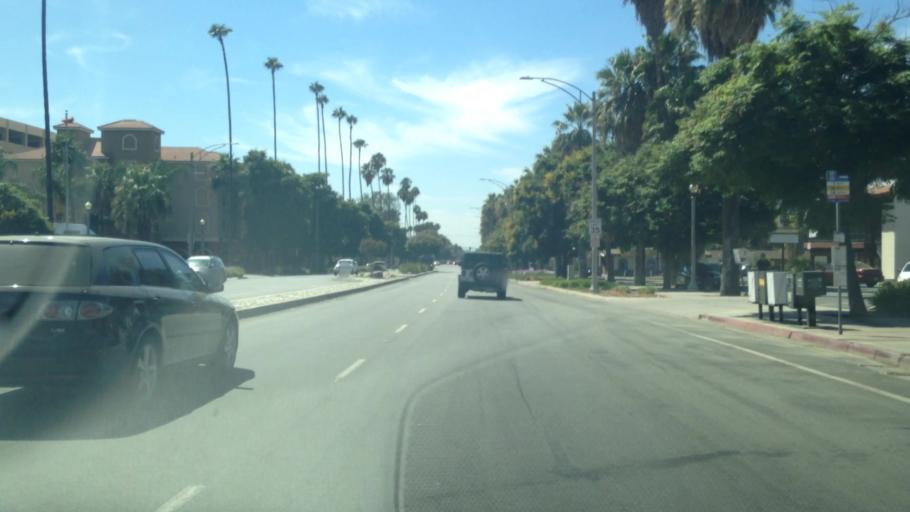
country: US
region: California
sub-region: Riverside County
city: Highgrove
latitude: 33.9758
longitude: -117.3402
